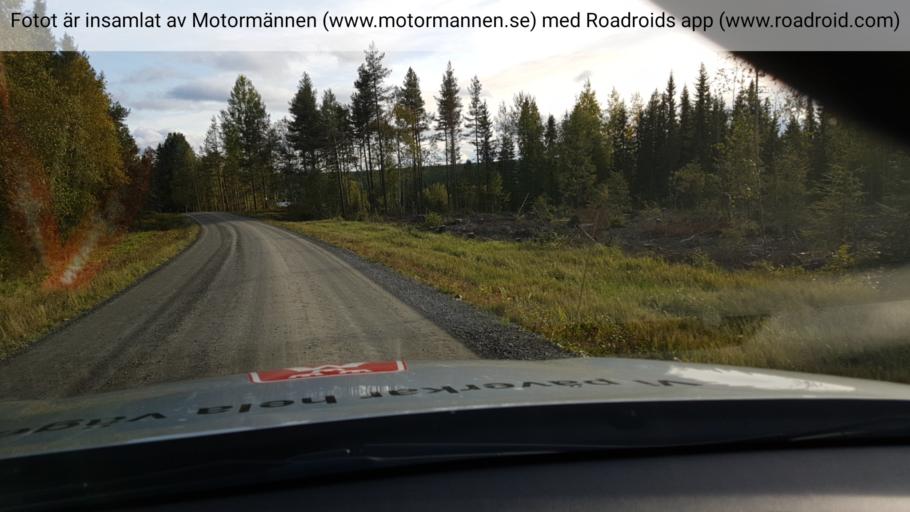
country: SE
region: Jaemtland
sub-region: Krokoms Kommun
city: Krokom
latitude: 63.6796
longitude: 14.5779
